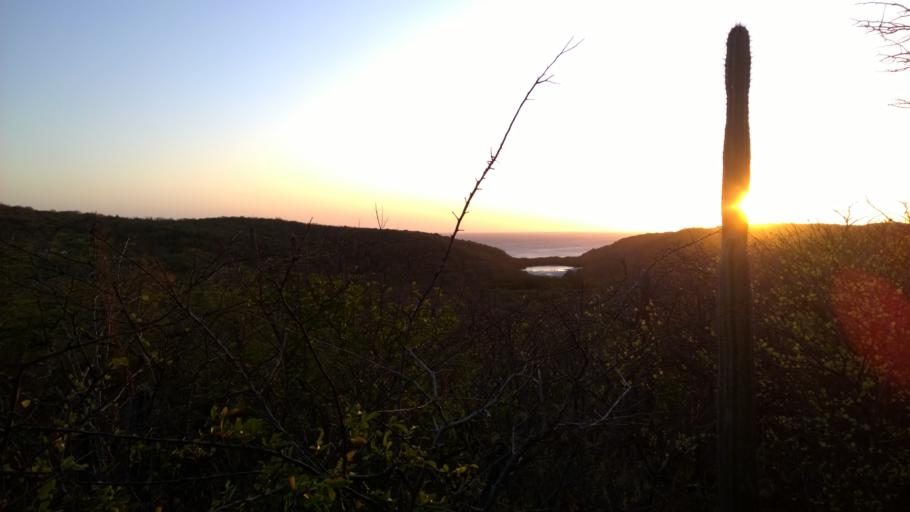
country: CW
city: Dorp Soto
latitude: 12.2596
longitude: -69.1083
